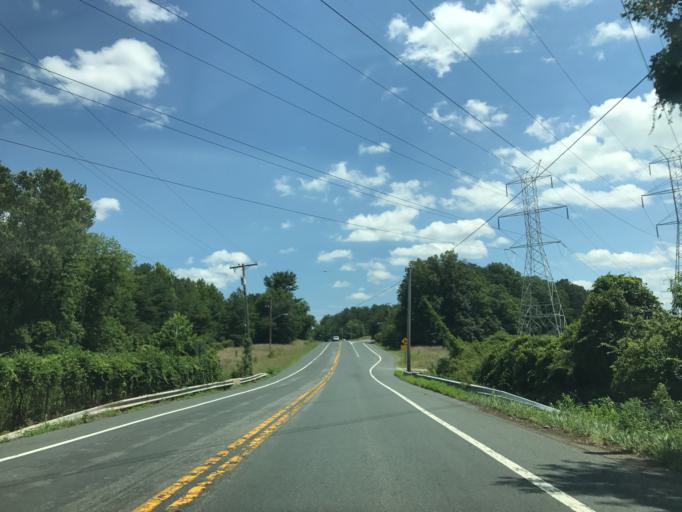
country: US
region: Maryland
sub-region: Prince George's County
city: Glenn Dale
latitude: 39.0333
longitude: -76.7881
